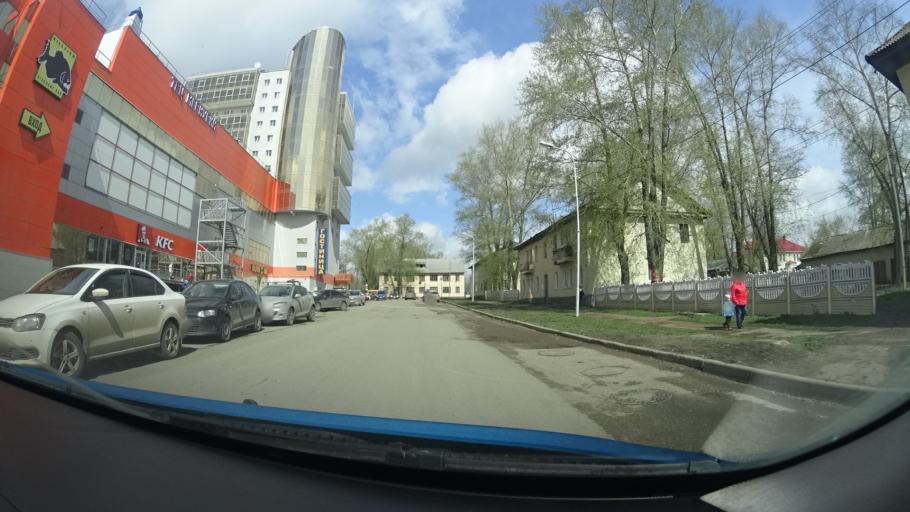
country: RU
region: Bashkortostan
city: Ufa
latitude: 54.8220
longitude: 56.0864
